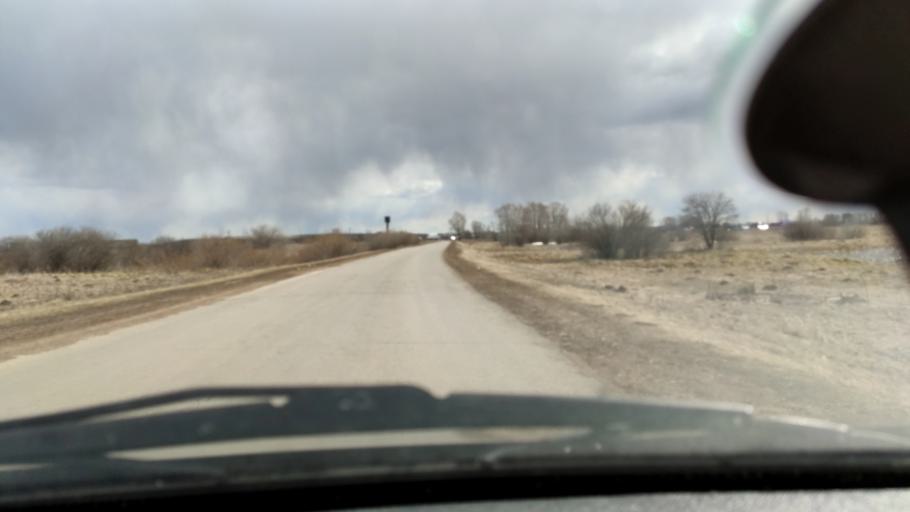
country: RU
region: Bashkortostan
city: Mikhaylovka
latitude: 54.9750
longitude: 55.7817
